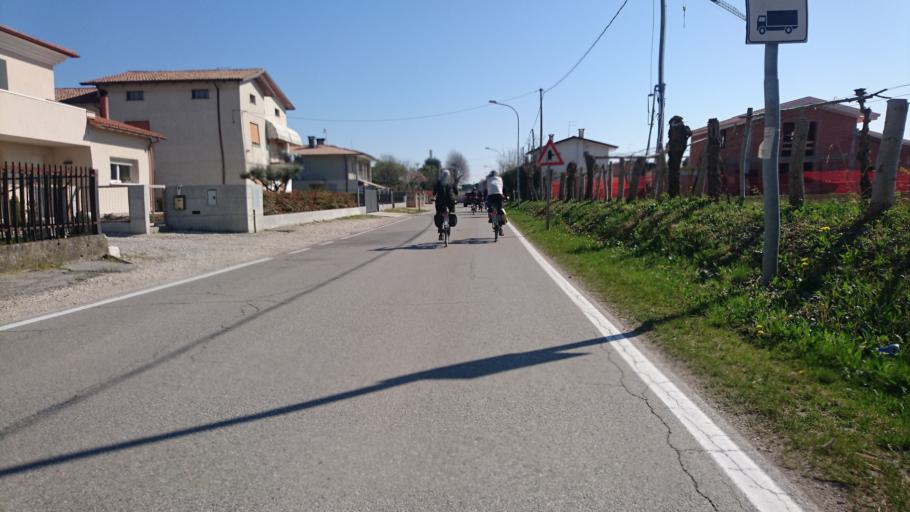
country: IT
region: Veneto
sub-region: Provincia di Padova
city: Cittadella
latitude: 45.6515
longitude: 11.7698
